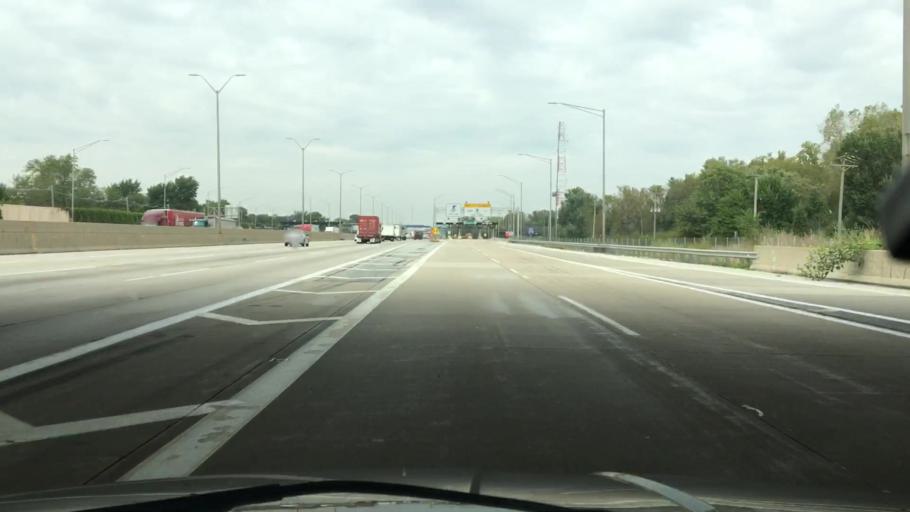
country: US
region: Illinois
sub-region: Cook County
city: University Park
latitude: 41.5863
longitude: -87.6808
